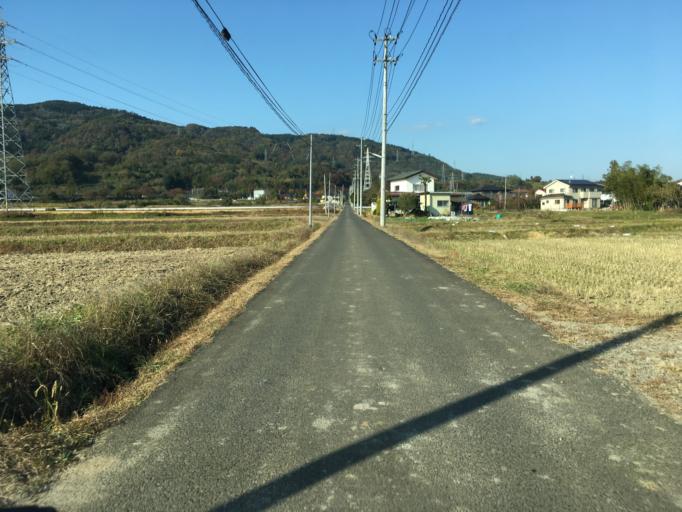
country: JP
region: Fukushima
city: Hobaramachi
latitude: 37.8298
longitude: 140.4943
